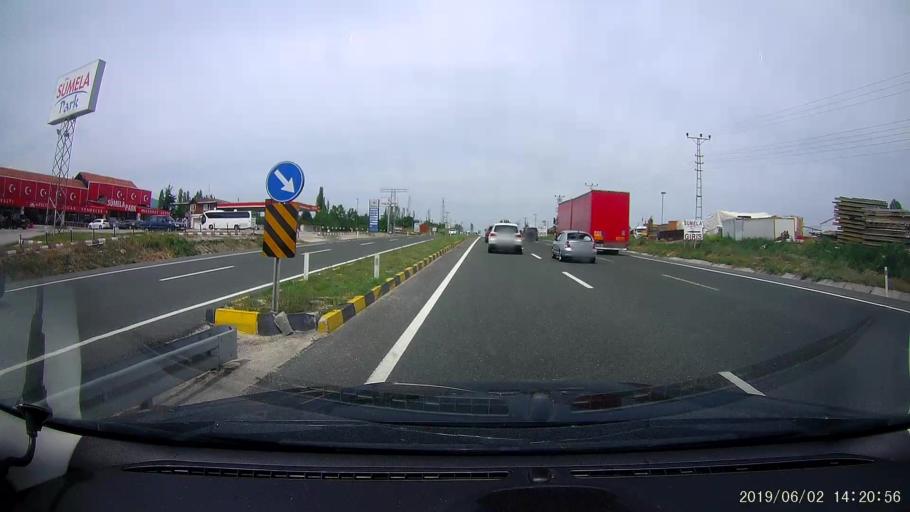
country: TR
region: Kastamonu
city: Tosya
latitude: 40.9741
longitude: 33.9980
